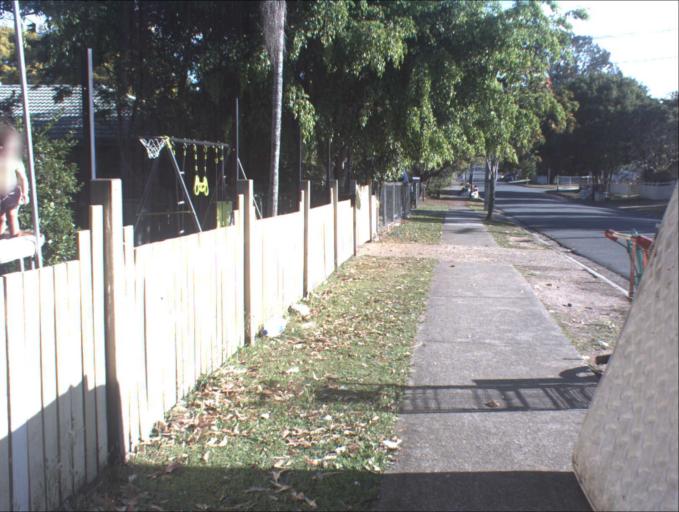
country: AU
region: Queensland
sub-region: Logan
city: Slacks Creek
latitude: -27.6457
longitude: 153.1325
